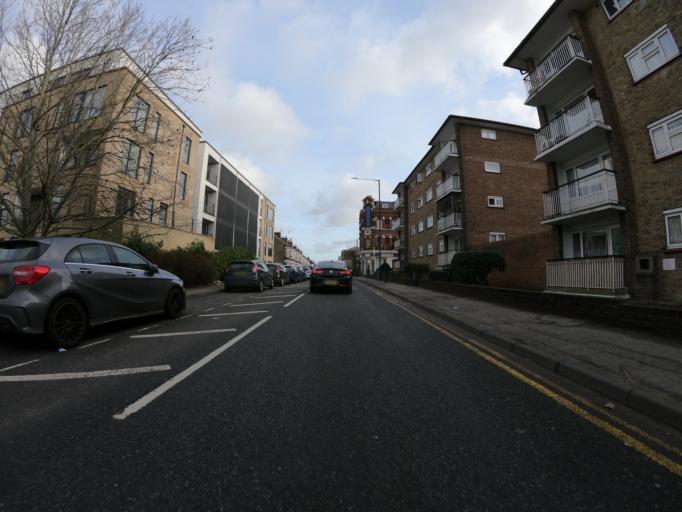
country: GB
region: England
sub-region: Kent
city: Gravesend
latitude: 51.4439
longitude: 0.3723
